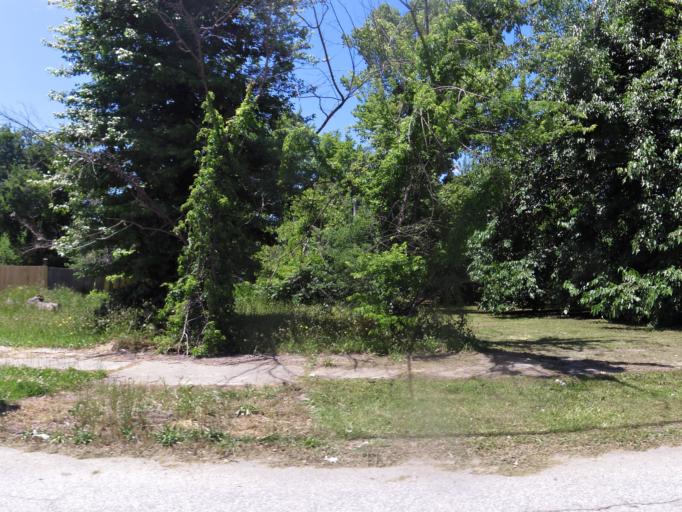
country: US
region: Georgia
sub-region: Richmond County
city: Augusta
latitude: 33.4654
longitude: -81.9680
